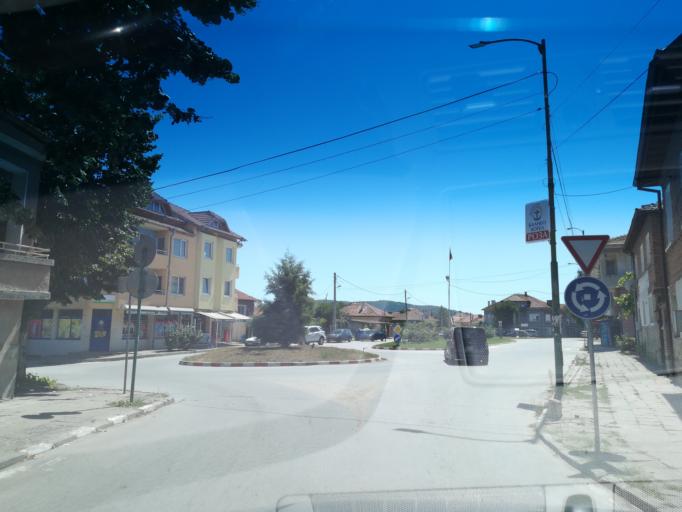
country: BG
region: Pazardzhik
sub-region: Obshtina Strelcha
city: Strelcha
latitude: 42.5039
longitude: 24.3217
